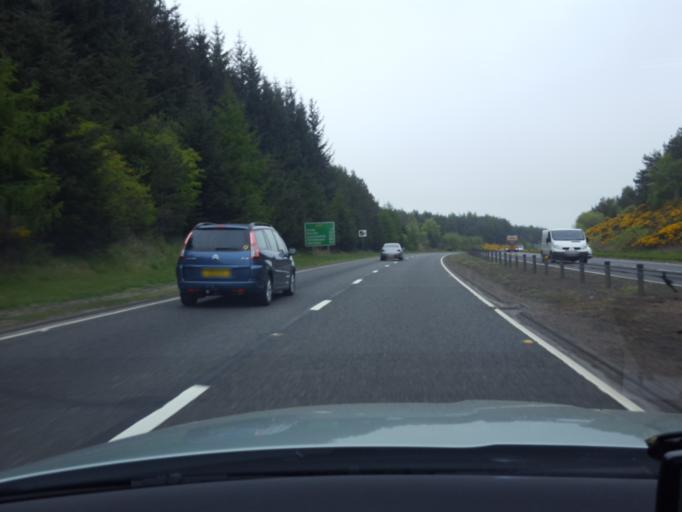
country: GB
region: Scotland
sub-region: Dundee City
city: Dundee
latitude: 56.5517
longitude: -2.9365
